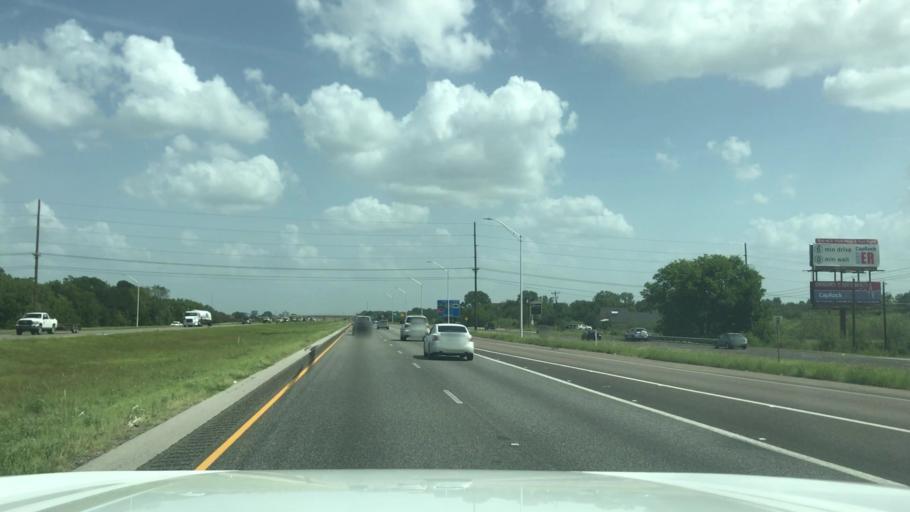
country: US
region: Texas
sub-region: Brazos County
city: College Station
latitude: 30.6485
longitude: -96.3166
